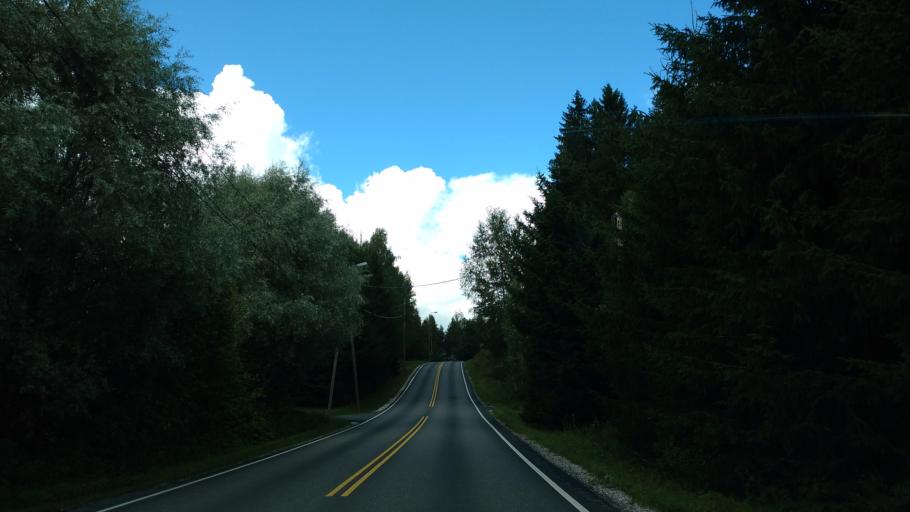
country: FI
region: Uusimaa
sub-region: Helsinki
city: Karjalohja
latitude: 60.2316
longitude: 23.7029
